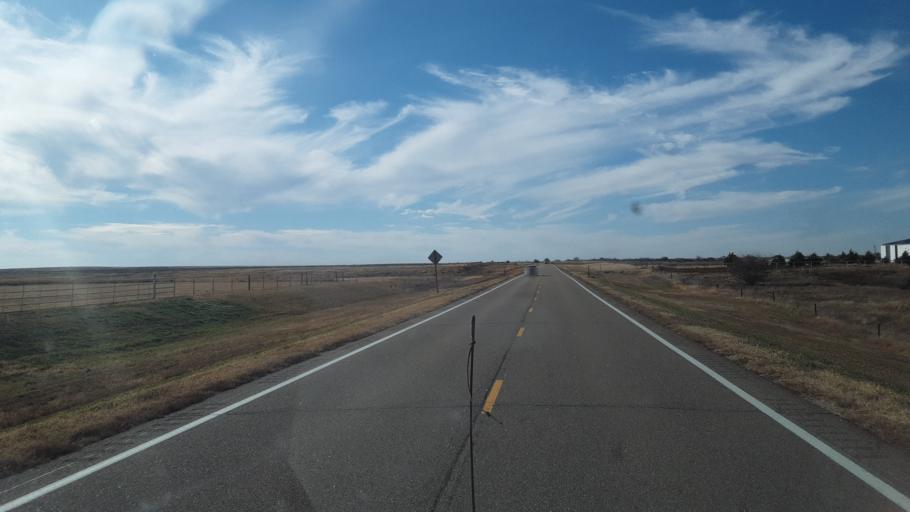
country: US
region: Kansas
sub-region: Edwards County
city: Kinsley
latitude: 38.1897
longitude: -99.5344
